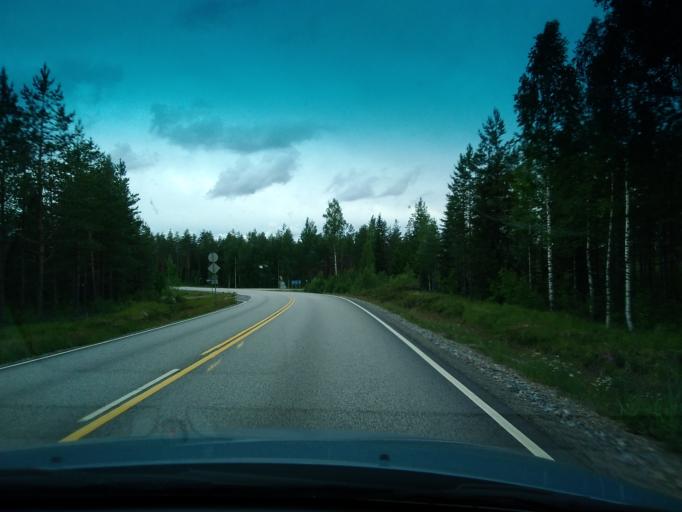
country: FI
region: Central Finland
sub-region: Keuruu
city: Multia
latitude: 62.4672
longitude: 24.7071
